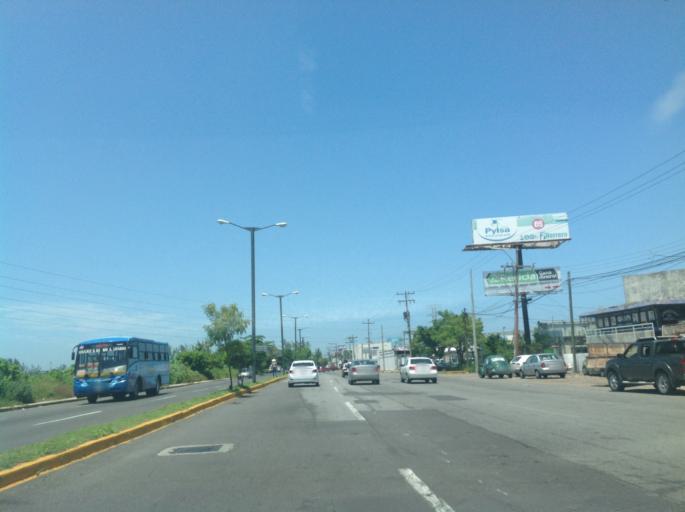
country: MX
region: Veracruz
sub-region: Veracruz
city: Hacienda Sotavento
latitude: 19.1435
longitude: -96.1460
